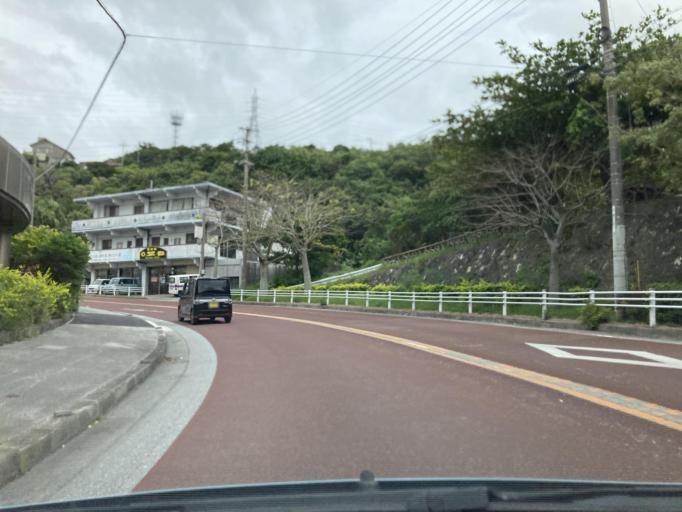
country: JP
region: Okinawa
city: Ginowan
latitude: 26.2359
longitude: 127.7539
